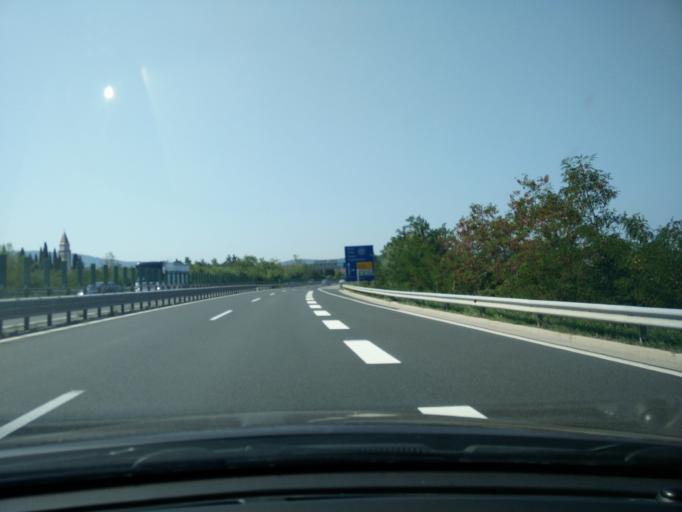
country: SI
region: Koper-Capodistria
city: Prade
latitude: 45.5507
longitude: 13.7739
